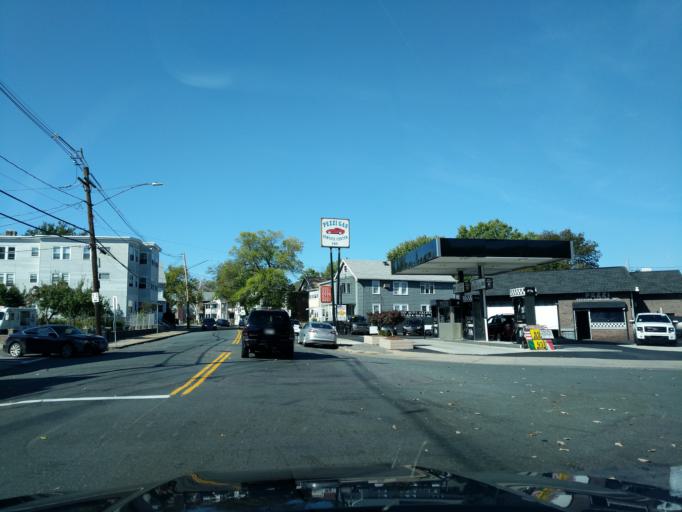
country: US
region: Massachusetts
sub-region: Suffolk County
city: Chelsea
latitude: 42.4095
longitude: -71.0300
